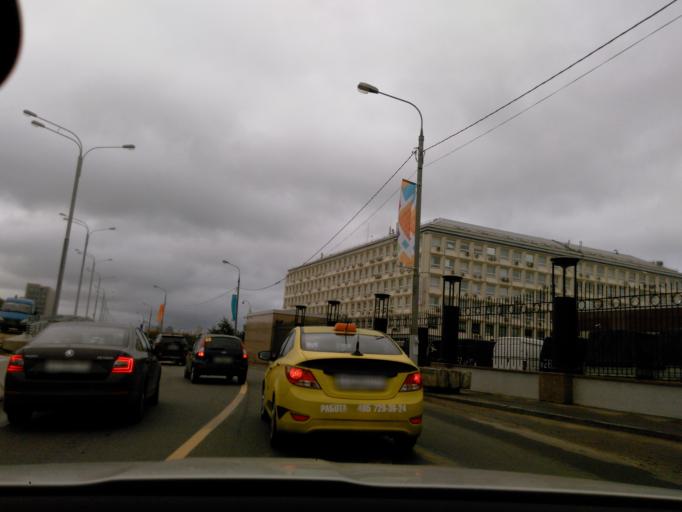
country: RU
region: Moscow
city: Strogino
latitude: 55.8256
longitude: 37.4279
